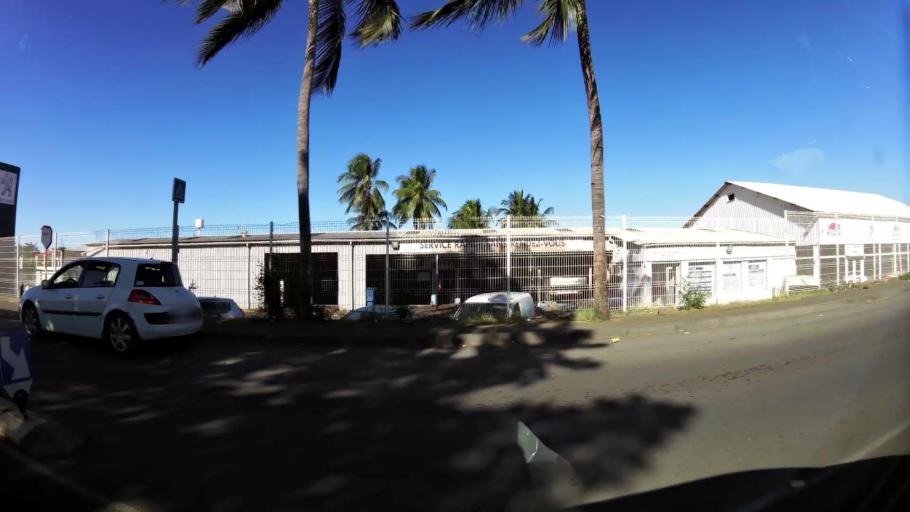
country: YT
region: Mamoudzou
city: Mamoudzou
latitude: -12.7704
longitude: 45.2238
